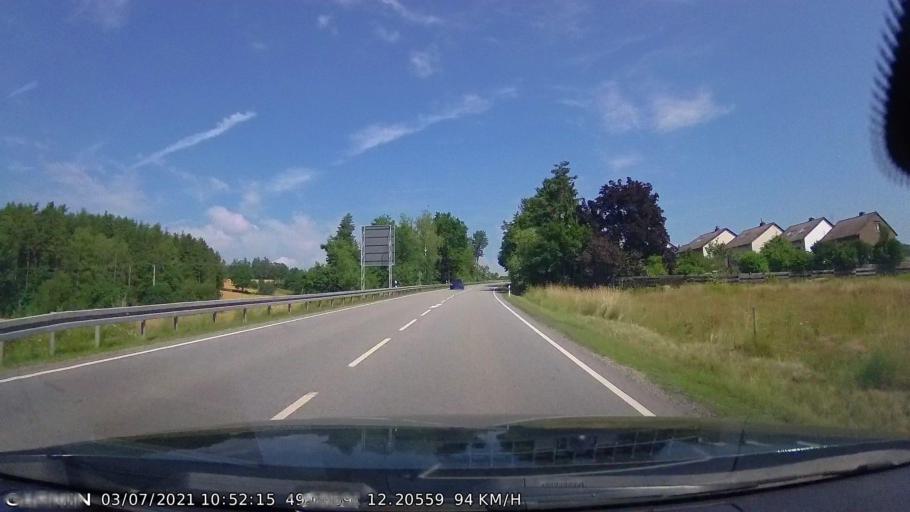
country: DE
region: Bavaria
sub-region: Upper Palatinate
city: Bechtsrieth
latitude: 49.6470
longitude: 12.2055
